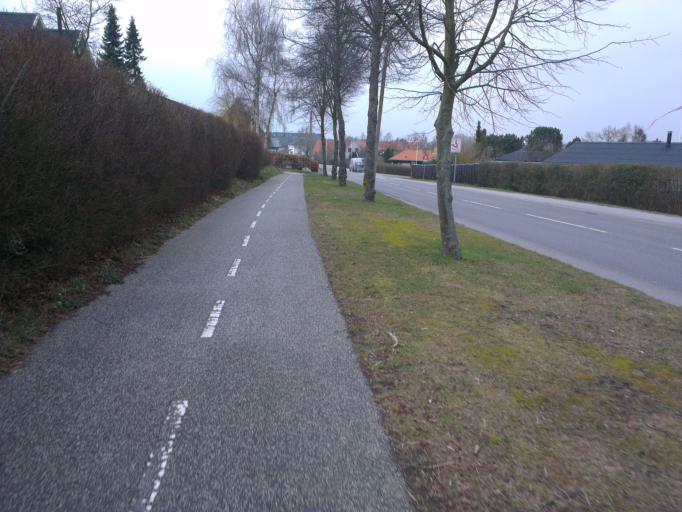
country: DK
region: Capital Region
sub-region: Frederikssund Kommune
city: Slangerup
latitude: 55.8408
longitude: 12.1755
